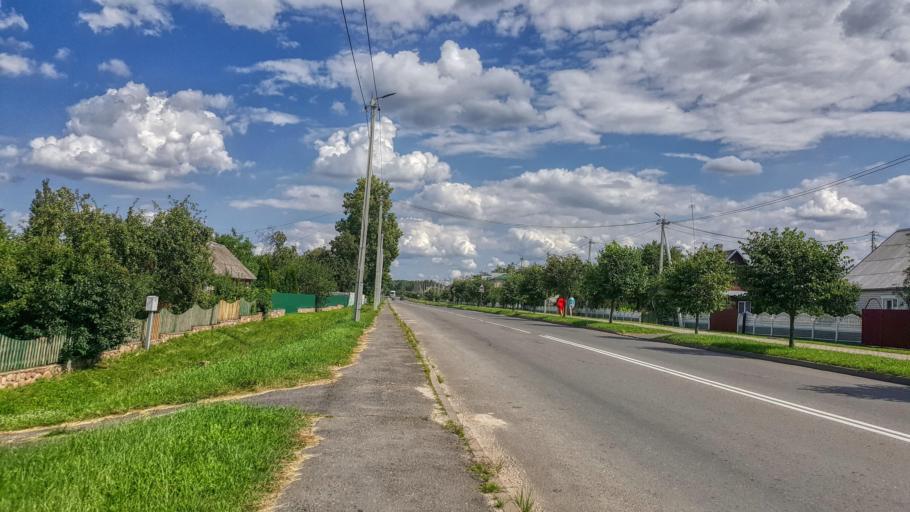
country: BY
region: Brest
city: Kamyanyets
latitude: 52.3966
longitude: 23.8279
